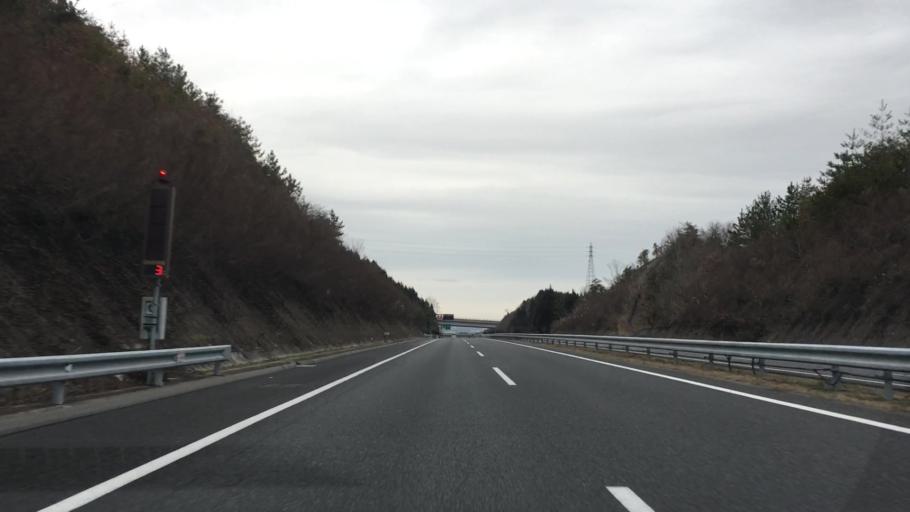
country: JP
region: Gifu
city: Toki
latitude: 35.3254
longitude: 137.1759
